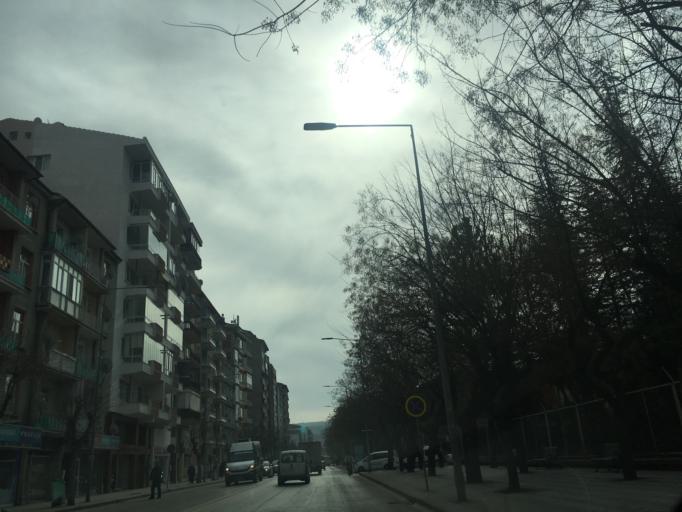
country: TR
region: Eskisehir
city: Eskisehir
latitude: 39.7728
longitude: 30.5137
